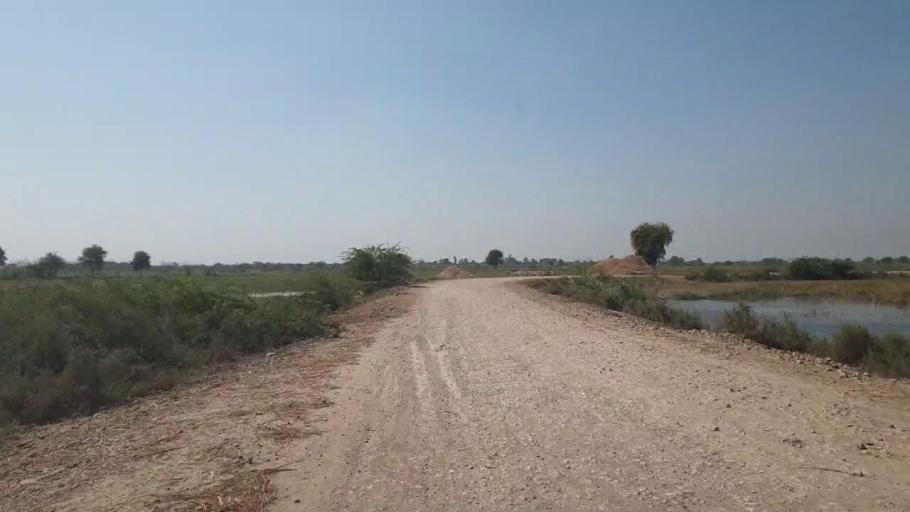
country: PK
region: Sindh
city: Talhar
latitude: 24.8336
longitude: 68.8047
